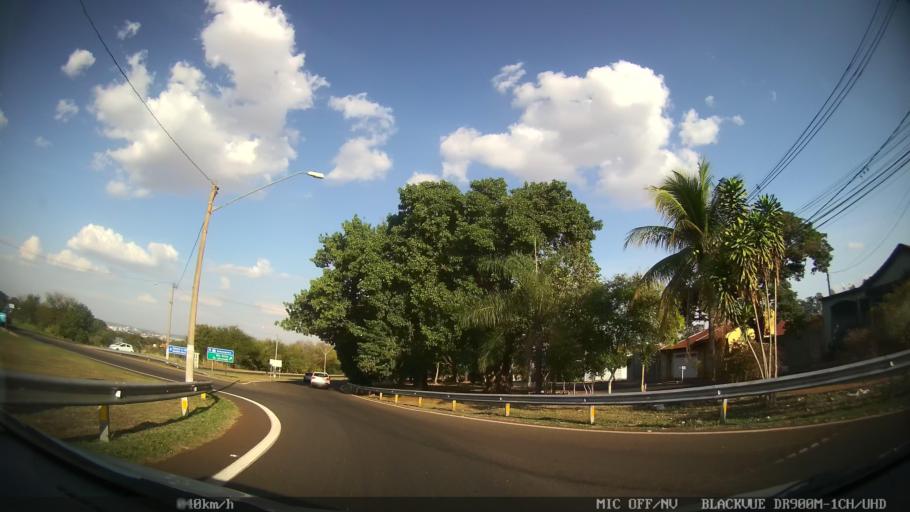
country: BR
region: Sao Paulo
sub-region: Ribeirao Preto
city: Ribeirao Preto
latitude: -21.1272
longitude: -47.8442
